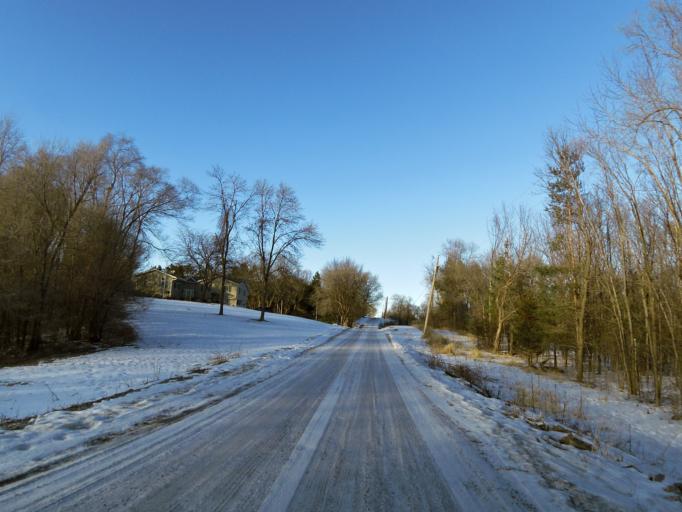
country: US
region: Wisconsin
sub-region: Pierce County
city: Prescott
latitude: 44.7904
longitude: -92.8273
